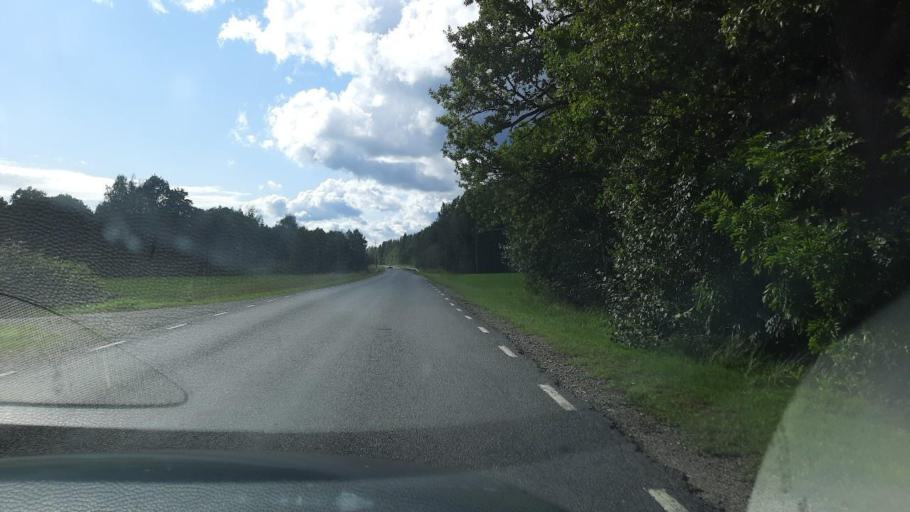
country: EE
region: Paernumaa
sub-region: Tootsi vald
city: Tootsi
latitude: 58.4982
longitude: 24.8665
